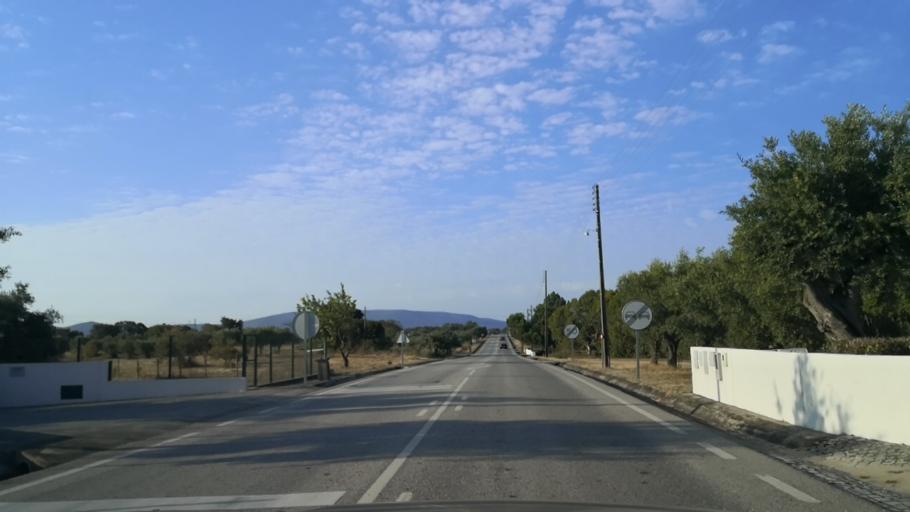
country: PT
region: Santarem
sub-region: Alcanena
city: Alcanena
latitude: 39.4148
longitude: -8.6372
